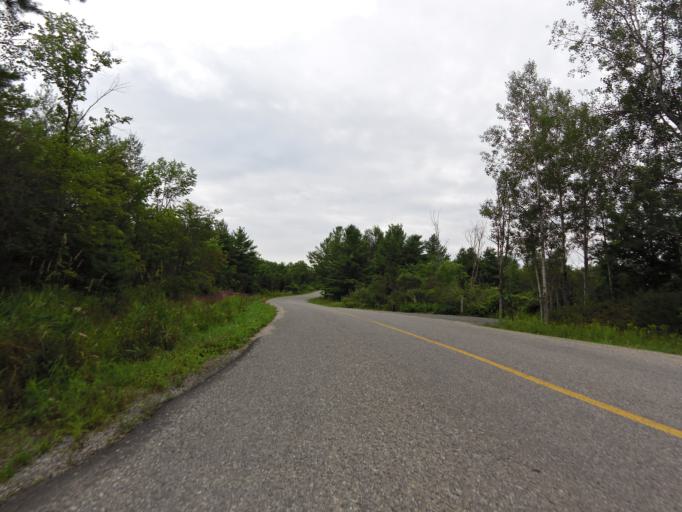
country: CA
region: Ontario
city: Kingston
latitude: 44.5959
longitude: -76.6400
